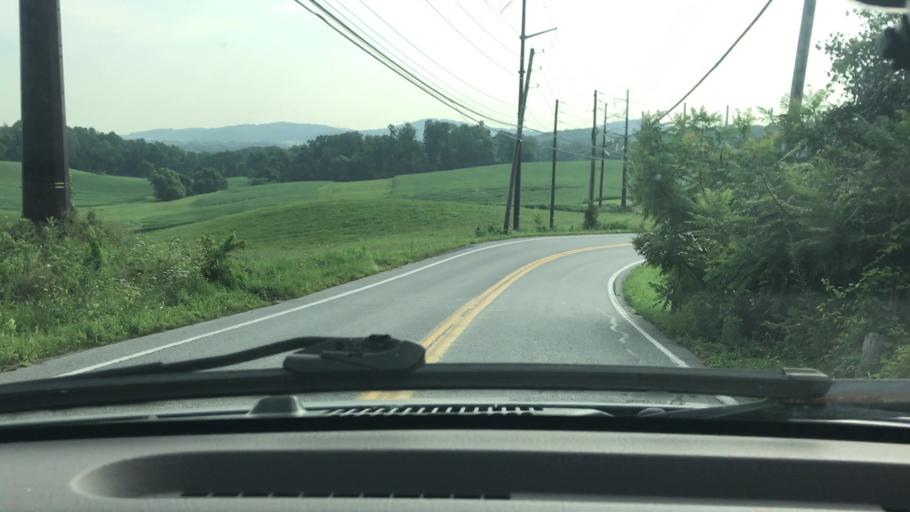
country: US
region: Pennsylvania
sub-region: Dauphin County
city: Middletown
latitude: 40.2219
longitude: -76.7501
